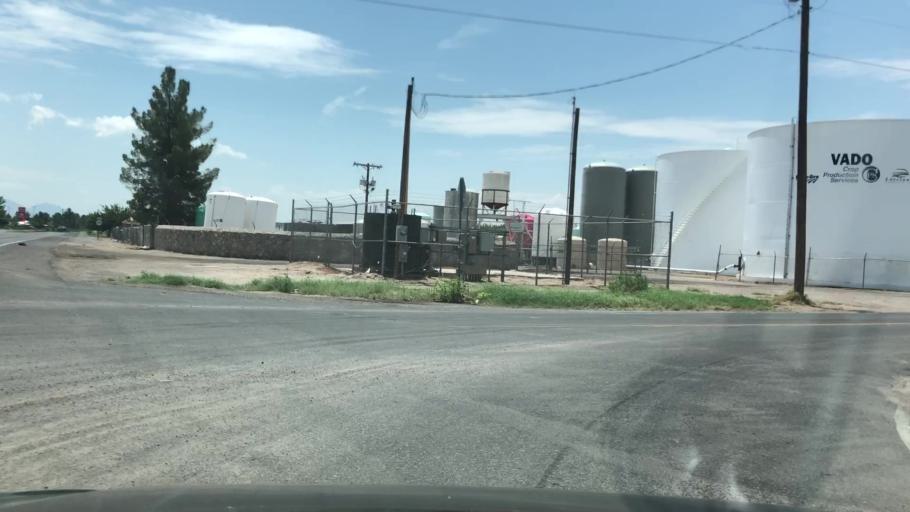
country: US
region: New Mexico
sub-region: Dona Ana County
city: Vado
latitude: 32.1157
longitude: -106.6651
